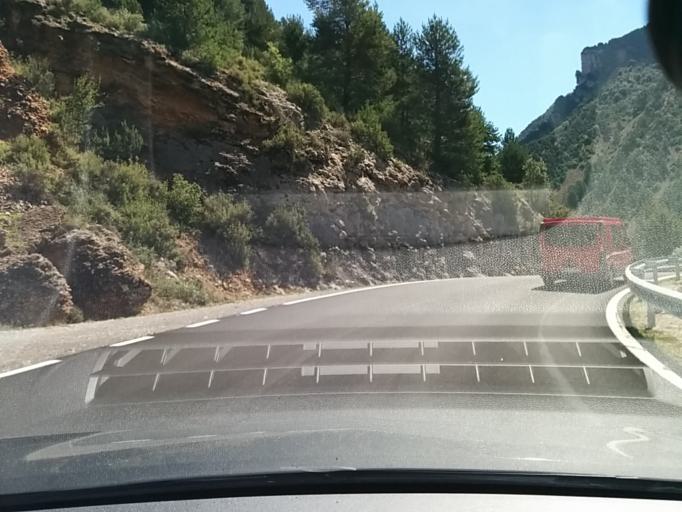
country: ES
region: Aragon
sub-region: Provincia de Huesca
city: Boltana
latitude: 42.4672
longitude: 0.0018
